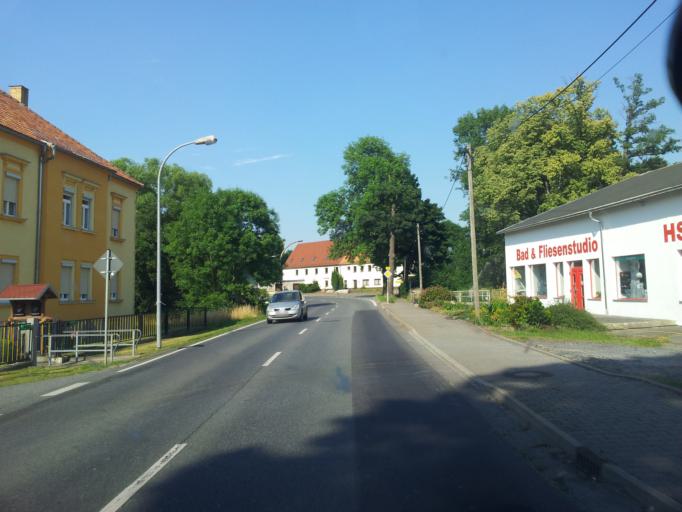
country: DE
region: Saxony
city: Konigsbruck
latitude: 51.2979
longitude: 13.9132
